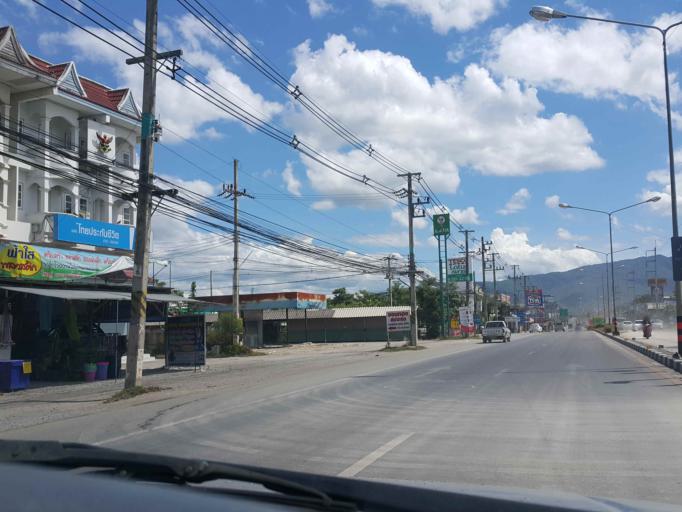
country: TH
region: Chiang Mai
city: Chom Thong
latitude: 18.4362
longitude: 98.6871
